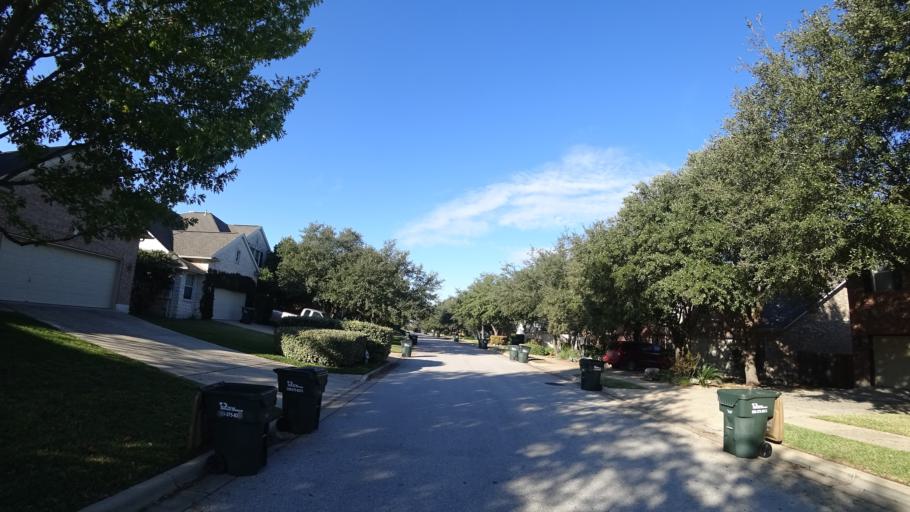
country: US
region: Texas
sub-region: Travis County
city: Hudson Bend
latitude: 30.3729
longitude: -97.8997
